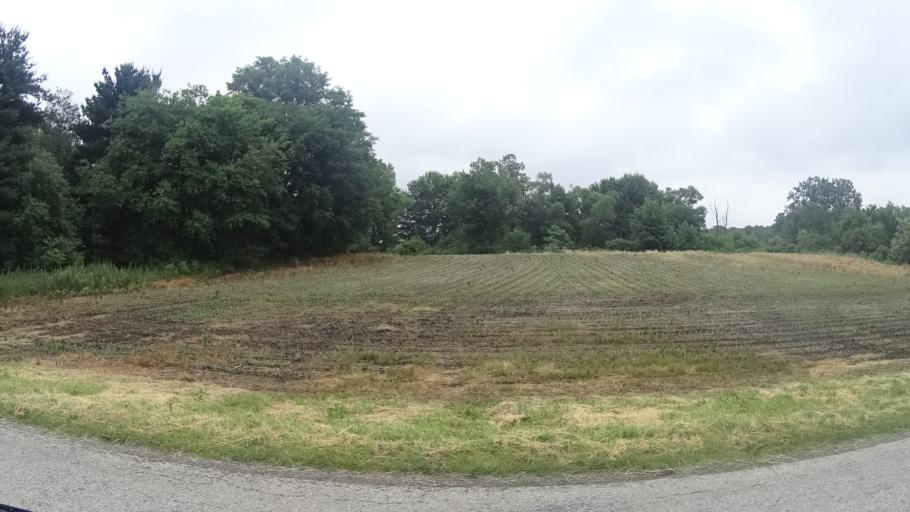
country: US
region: Ohio
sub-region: Erie County
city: Milan
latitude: 41.2915
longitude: -82.5510
